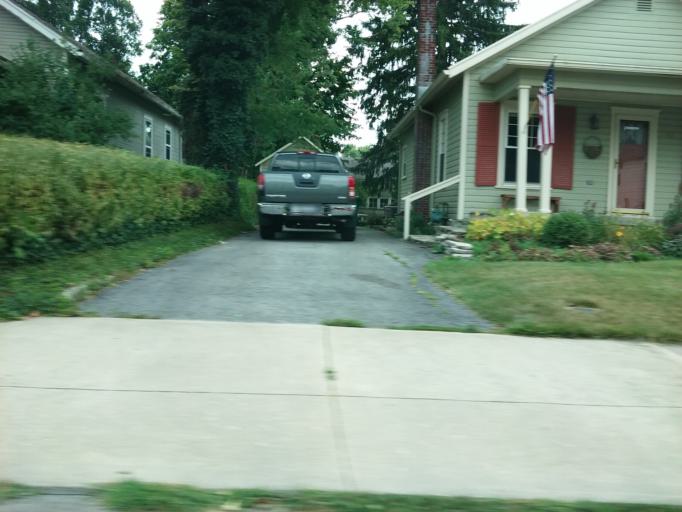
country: US
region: Ohio
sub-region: Hancock County
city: Findlay
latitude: 41.0440
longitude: -83.6368
